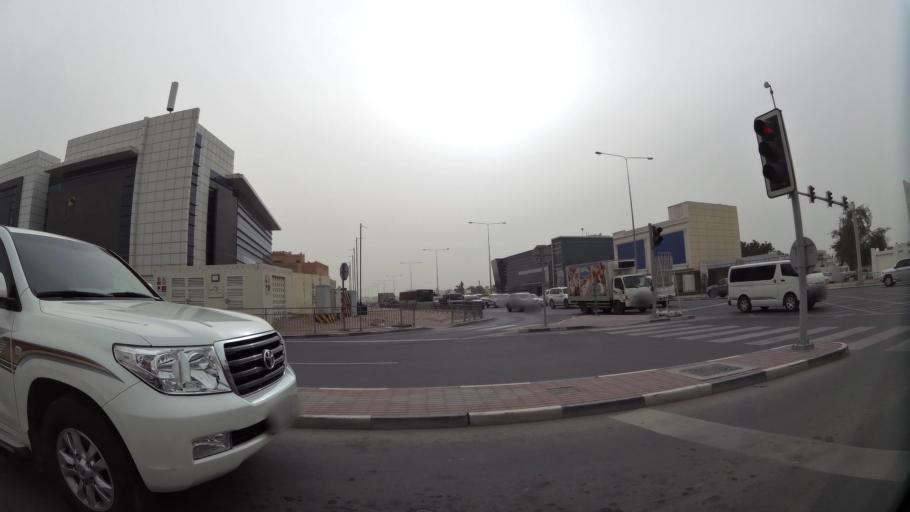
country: QA
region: Baladiyat ad Dawhah
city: Doha
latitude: 25.2579
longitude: 51.4980
